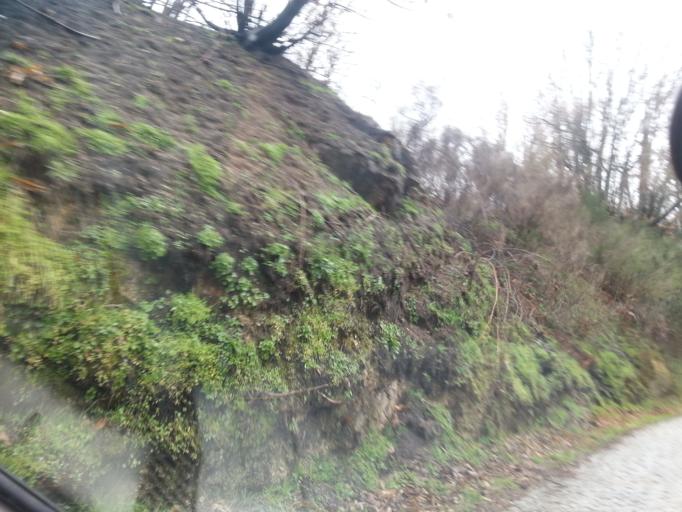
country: PT
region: Guarda
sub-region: Celorico da Beira
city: Celorico da Beira
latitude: 40.5422
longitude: -7.4582
